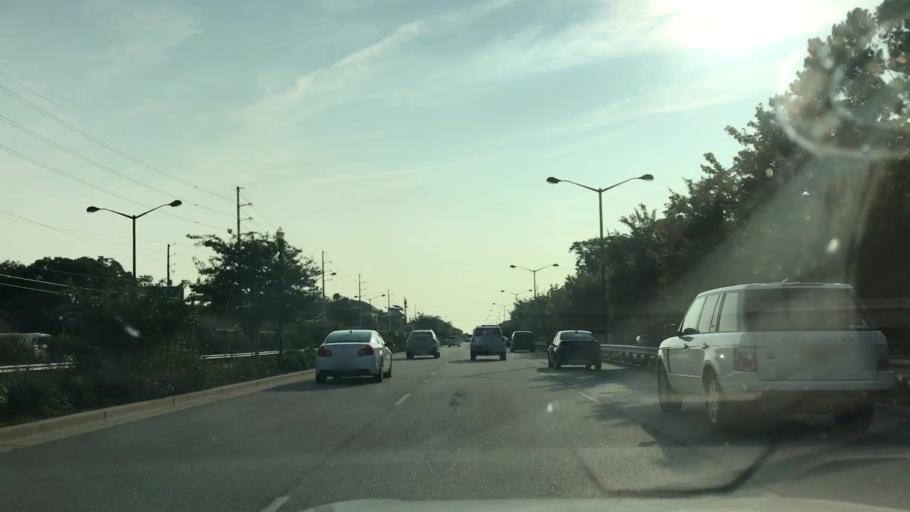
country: US
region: South Carolina
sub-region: Charleston County
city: Mount Pleasant
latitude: 32.8059
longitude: -79.8865
